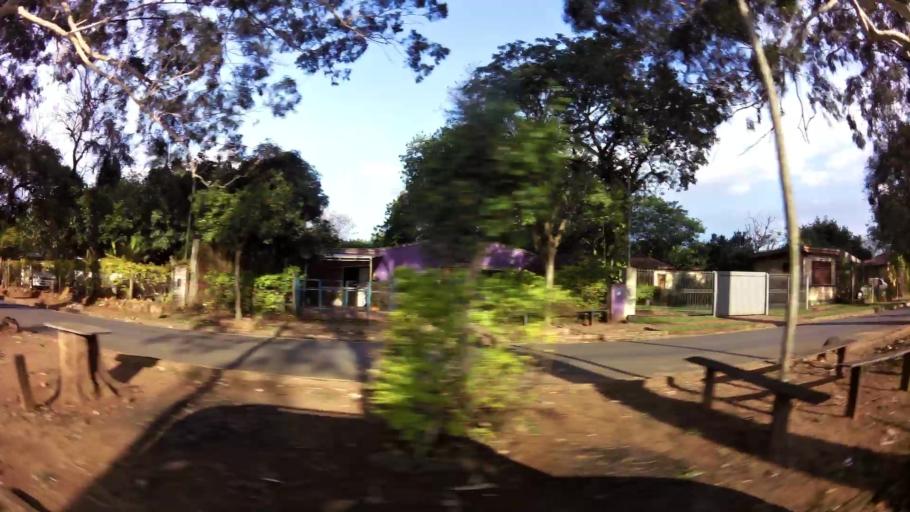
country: PY
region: Central
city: Fernando de la Mora
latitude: -25.3570
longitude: -57.5218
